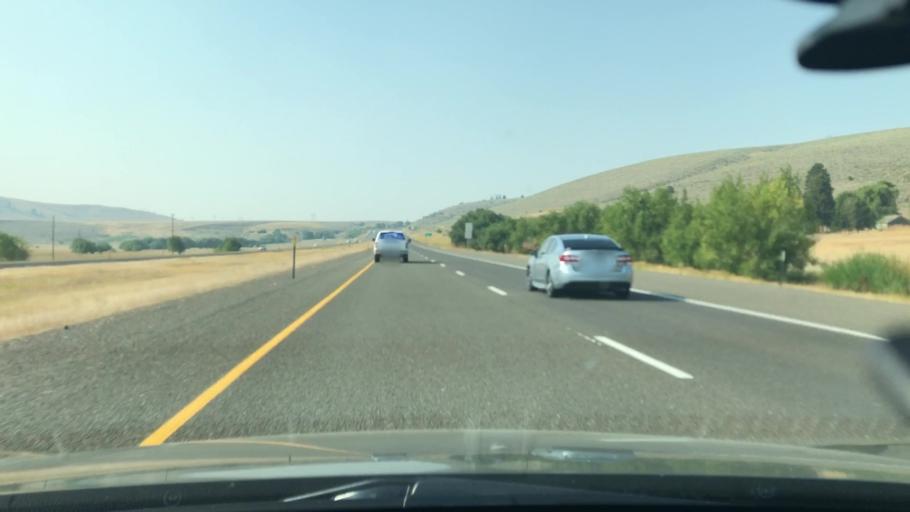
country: US
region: Oregon
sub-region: Union County
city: Union
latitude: 45.1334
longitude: -117.9659
